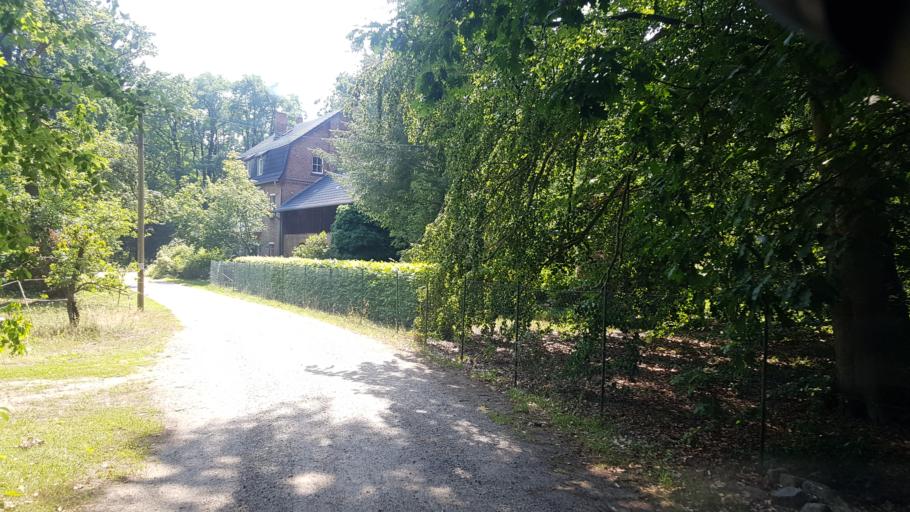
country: DE
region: Brandenburg
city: Cottbus
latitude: 51.6816
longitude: 14.4084
